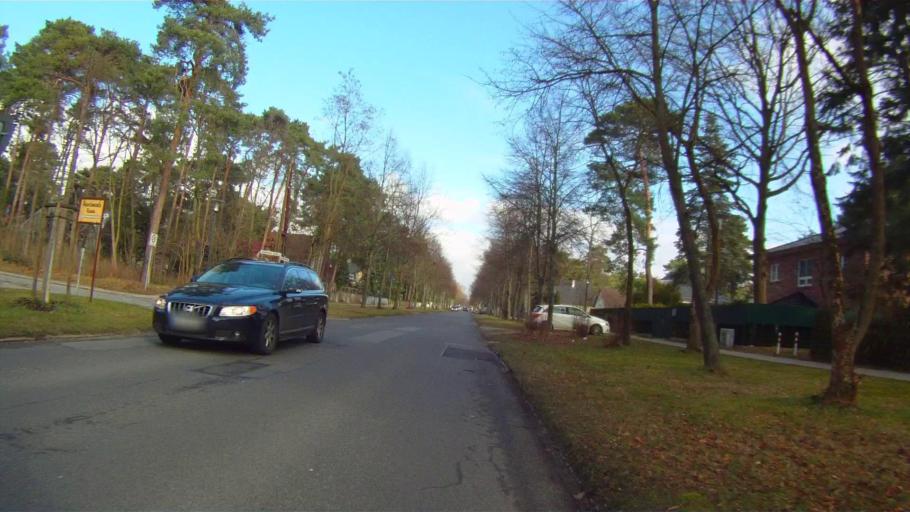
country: DE
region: Berlin
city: Friedrichshagen
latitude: 52.4779
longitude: 13.6207
